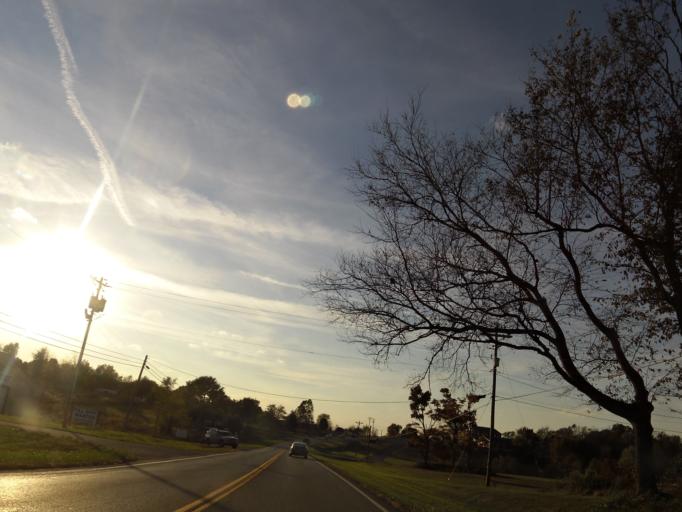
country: US
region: Kentucky
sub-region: Garrard County
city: Lancaster
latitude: 37.6739
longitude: -84.6410
